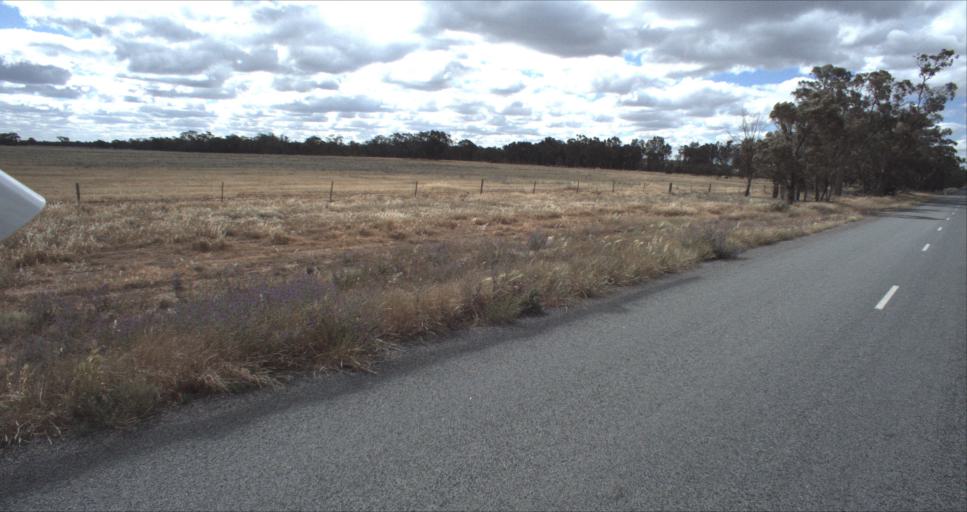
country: AU
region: New South Wales
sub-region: Leeton
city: Leeton
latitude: -34.6689
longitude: 146.3478
